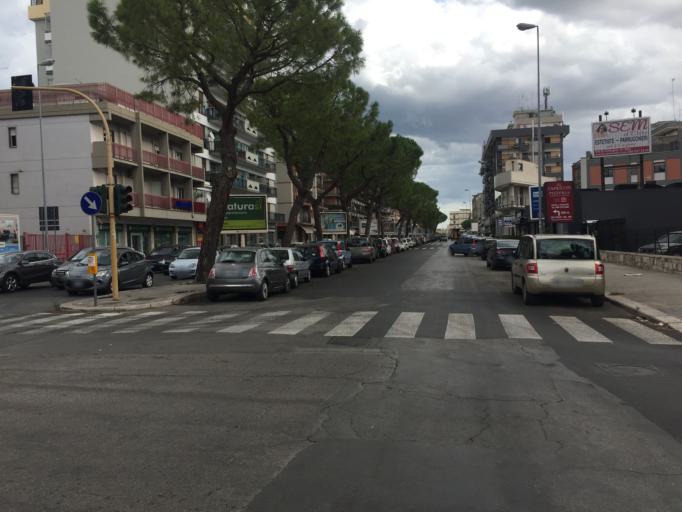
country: IT
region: Apulia
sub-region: Provincia di Bari
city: Bari
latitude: 41.1071
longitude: 16.8599
